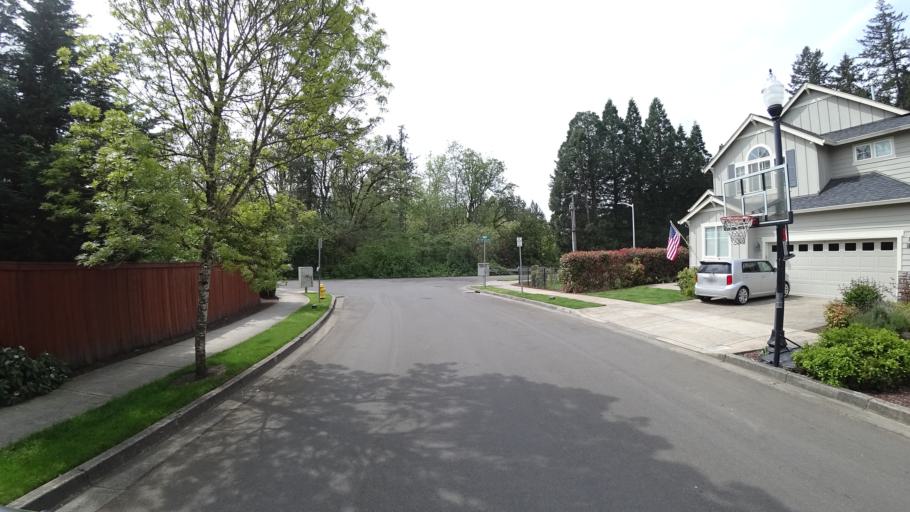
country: US
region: Oregon
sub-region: Washington County
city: Hillsboro
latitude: 45.5469
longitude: -123.0010
